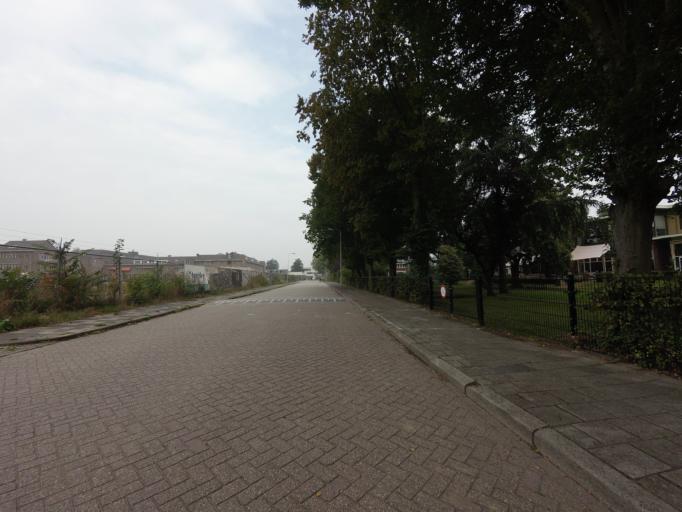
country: NL
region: Overijssel
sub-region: Gemeente Deventer
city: Deventer
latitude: 52.2620
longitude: 6.1709
